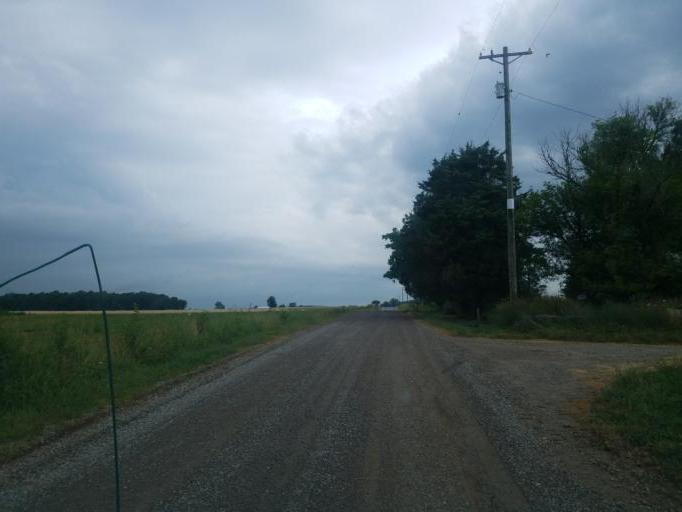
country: US
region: Ohio
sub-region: Defiance County
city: Hicksville
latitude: 41.3158
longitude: -84.8039
